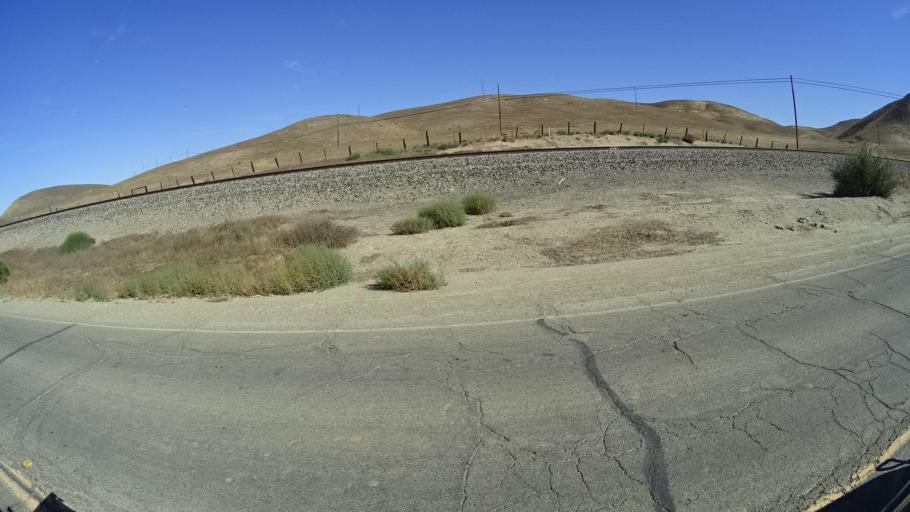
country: US
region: California
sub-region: Monterey County
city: King City
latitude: 36.1044
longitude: -120.9832
